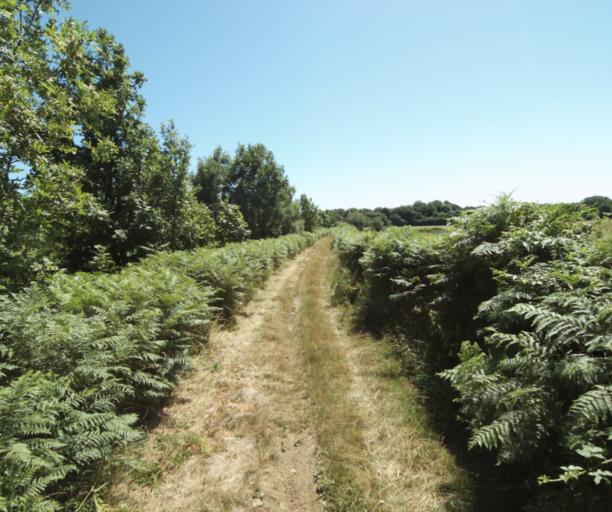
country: FR
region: Midi-Pyrenees
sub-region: Departement du Tarn
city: Dourgne
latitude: 43.4345
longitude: 2.1549
